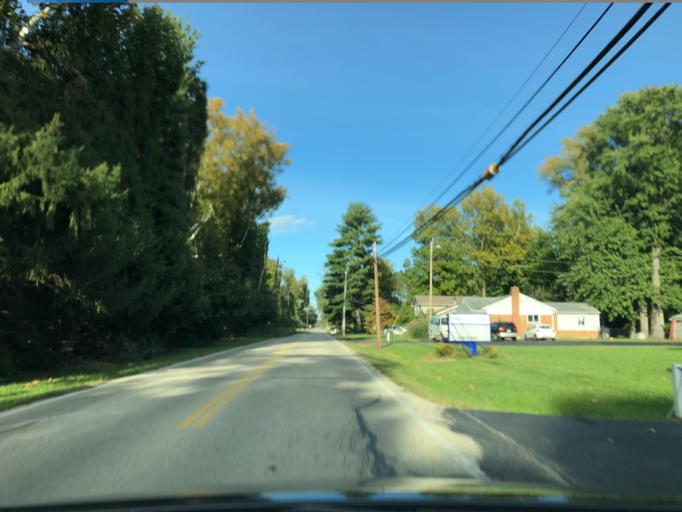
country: US
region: Ohio
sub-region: Hamilton County
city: Loveland
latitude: 39.2591
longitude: -84.2622
